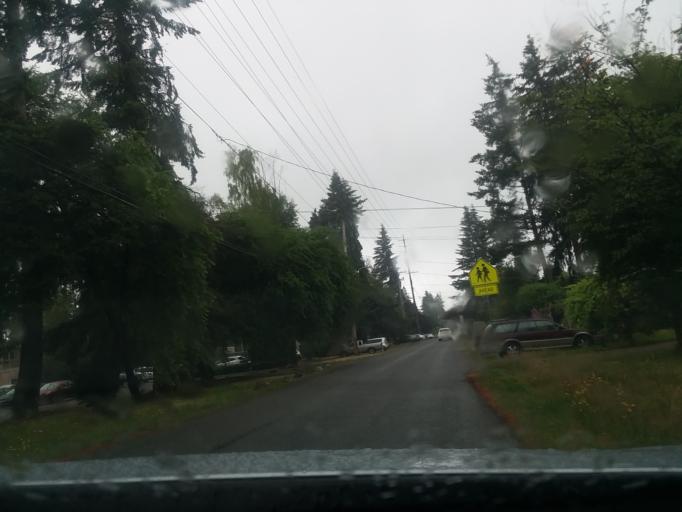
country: US
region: Washington
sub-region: King County
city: Shoreline
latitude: 47.7178
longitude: -122.3208
